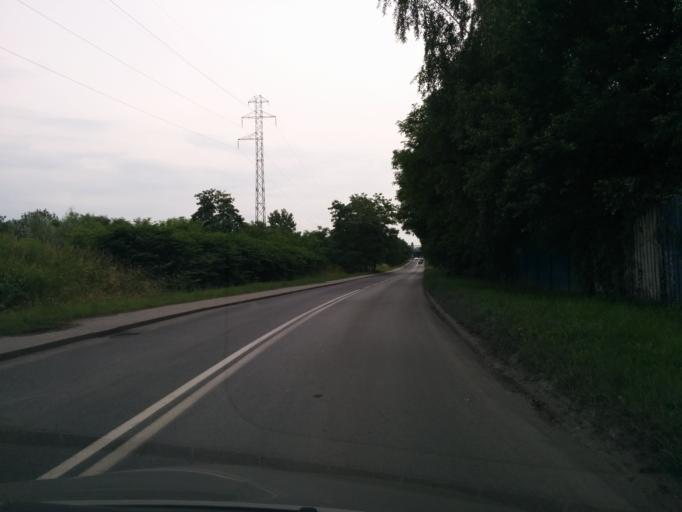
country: PL
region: Silesian Voivodeship
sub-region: Ruda Slaska
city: Ruda Slaska
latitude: 50.2626
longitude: 18.8385
